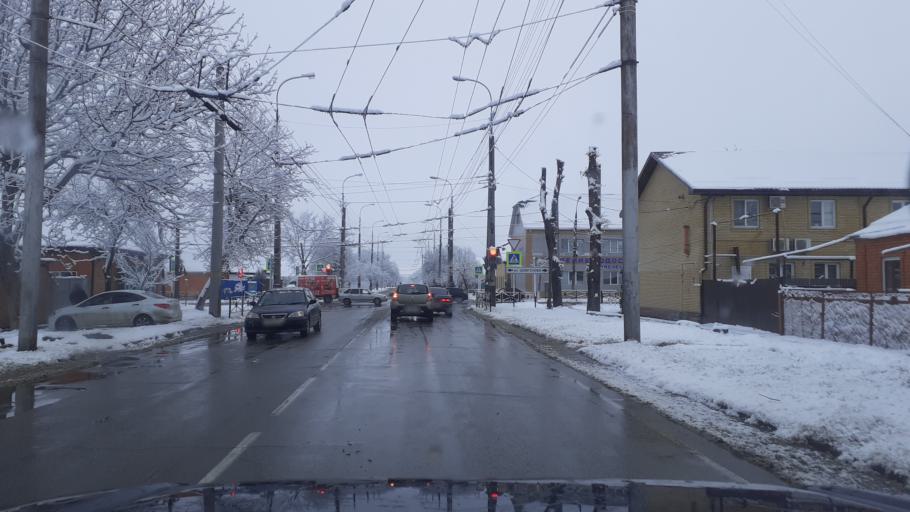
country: RU
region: Adygeya
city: Maykop
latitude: 44.6145
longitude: 40.1196
